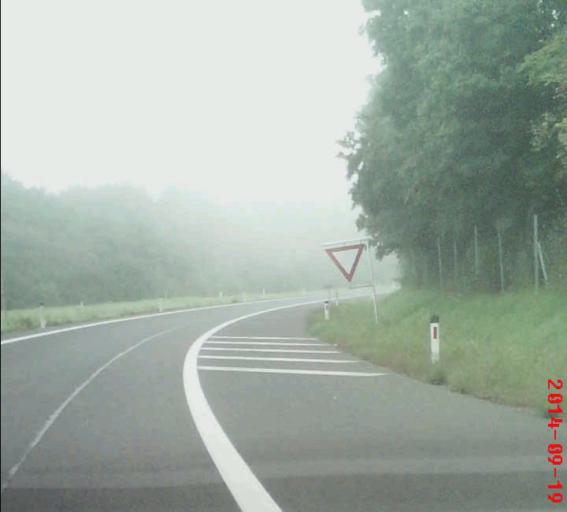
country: AT
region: Styria
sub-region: Politischer Bezirk Graz-Umgebung
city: Seiersberg
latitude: 47.0004
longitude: 15.4119
